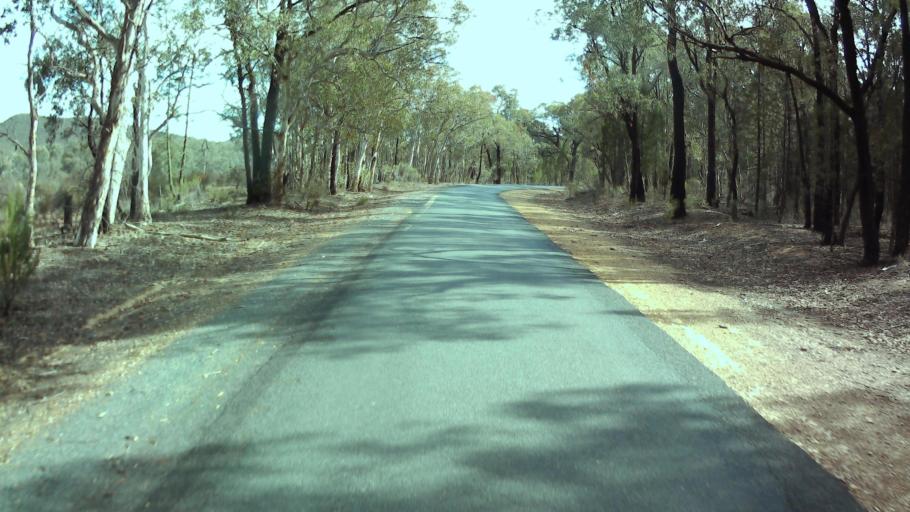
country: AU
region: New South Wales
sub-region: Weddin
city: Grenfell
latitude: -33.8588
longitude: 148.2153
